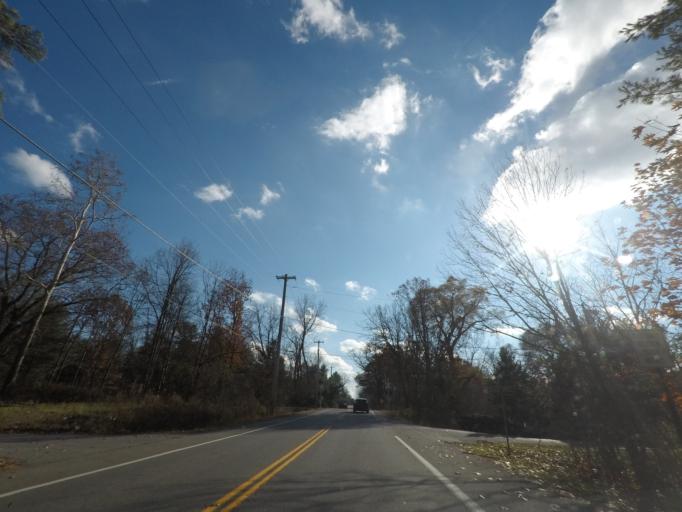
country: US
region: New York
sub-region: Schenectady County
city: East Glenville
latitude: 42.8886
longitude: -73.8884
